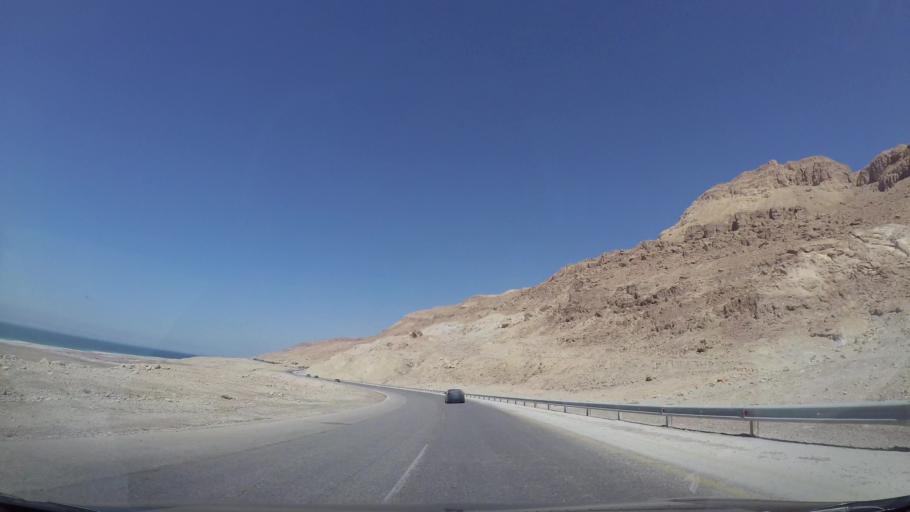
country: JO
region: Karak
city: Al Qasr
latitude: 31.3330
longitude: 35.5476
